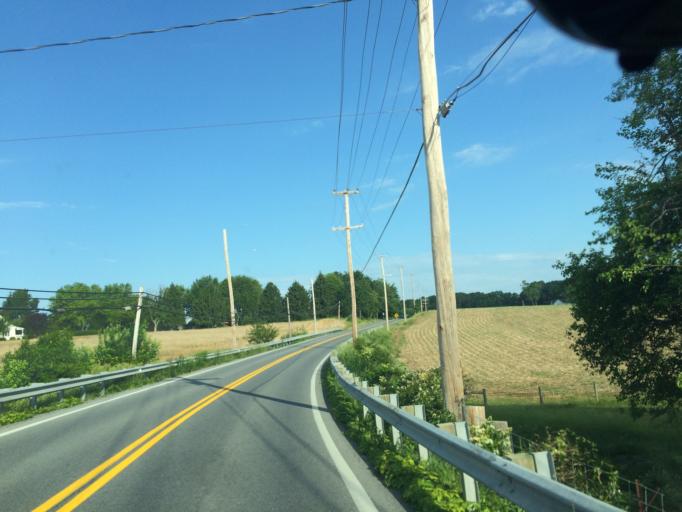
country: US
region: Maryland
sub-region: Carroll County
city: Sykesville
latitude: 39.3805
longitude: -76.9915
